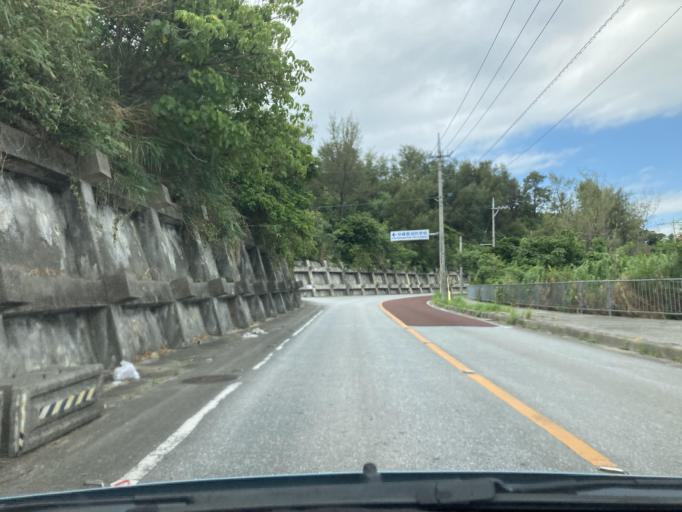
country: JP
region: Okinawa
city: Ginowan
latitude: 26.2666
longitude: 127.7858
